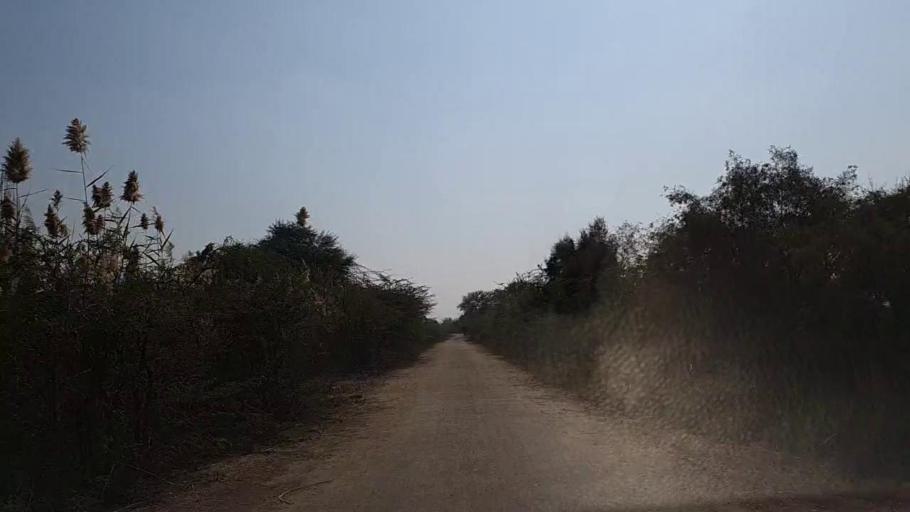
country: PK
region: Sindh
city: Jam Sahib
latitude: 26.2639
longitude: 68.5286
